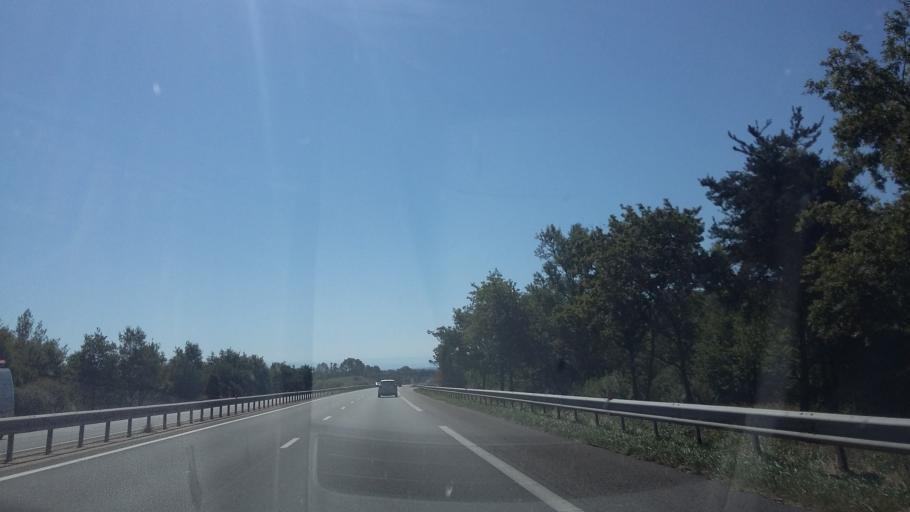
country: FR
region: Rhone-Alpes
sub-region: Departement de la Loire
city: Balbigny
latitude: 45.7683
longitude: 4.1581
